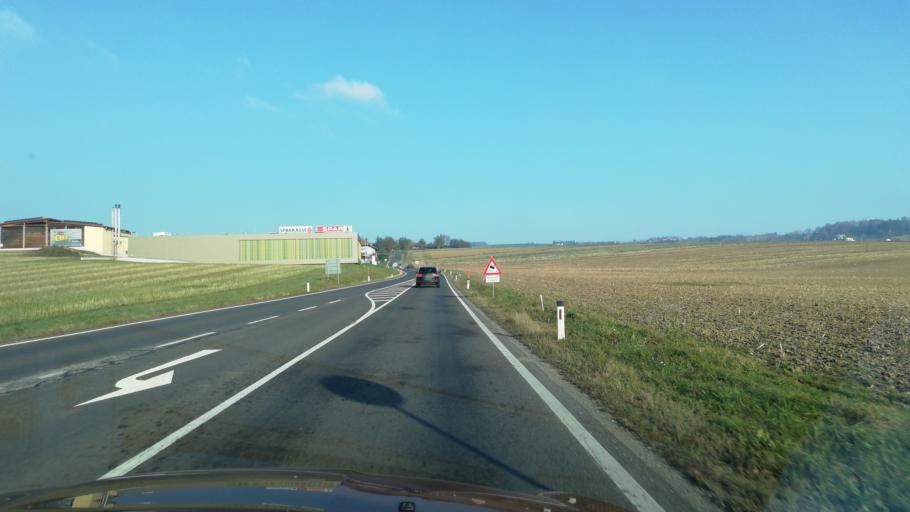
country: AT
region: Upper Austria
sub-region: Wels-Land
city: Buchkirchen
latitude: 48.2235
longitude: 14.0293
